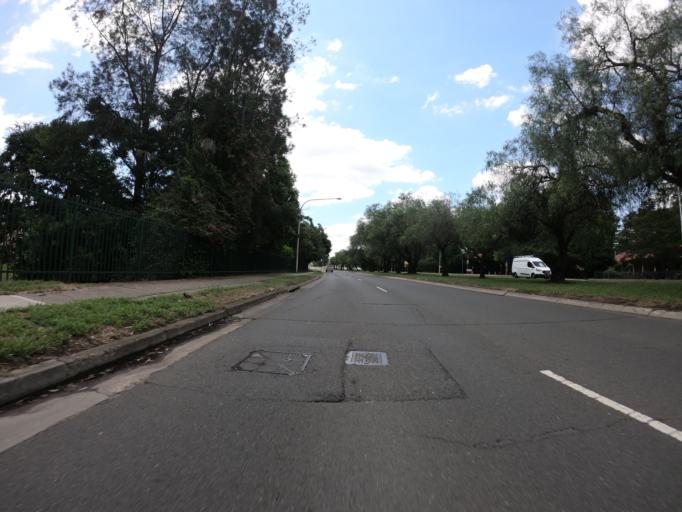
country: AU
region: New South Wales
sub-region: Penrith Municipality
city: Penrith
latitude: -33.7553
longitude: 150.6868
